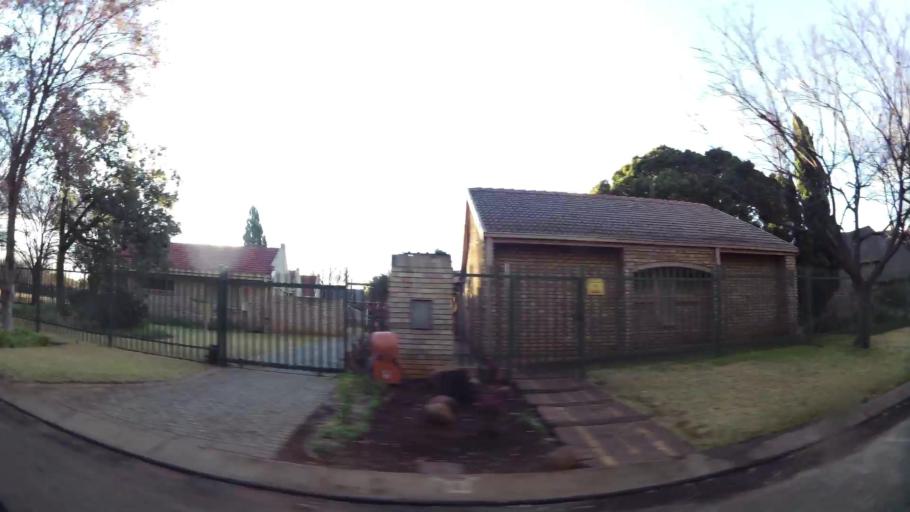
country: ZA
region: North-West
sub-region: Dr Kenneth Kaunda District Municipality
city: Potchefstroom
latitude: -26.6796
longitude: 27.1100
